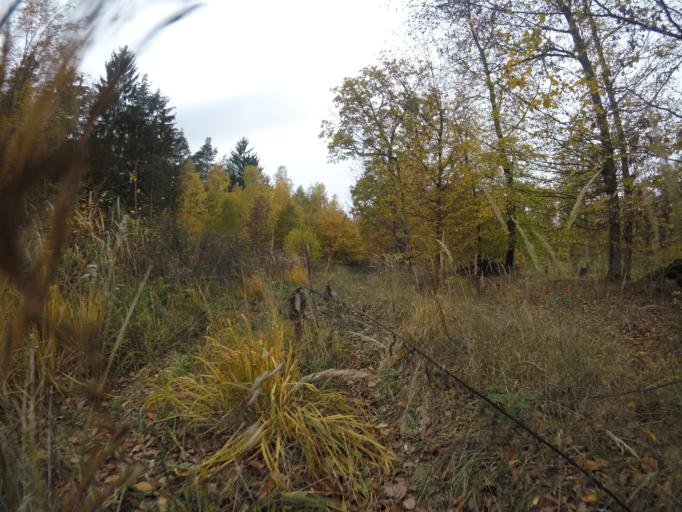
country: DE
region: Baden-Wuerttemberg
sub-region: Regierungsbezirk Stuttgart
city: Kirchberg an der Murr
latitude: 48.9795
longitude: 9.3498
